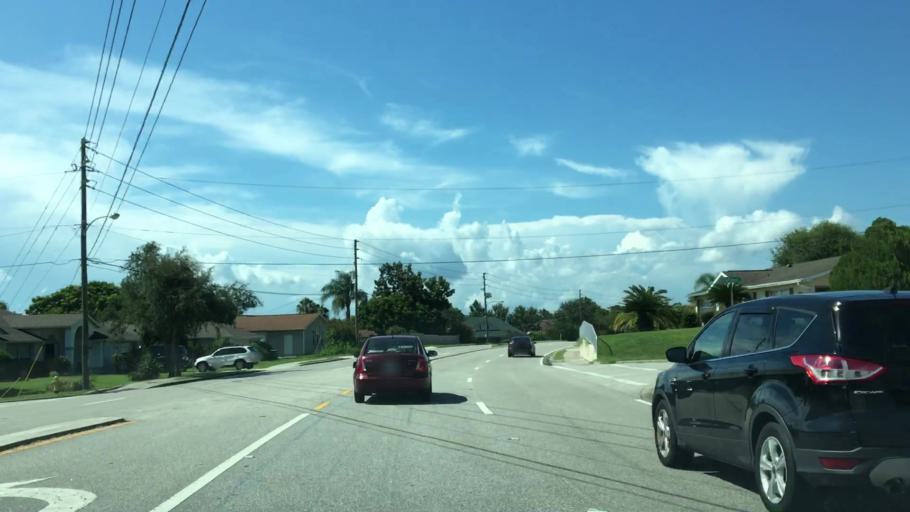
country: US
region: Florida
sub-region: Volusia County
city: Deltona
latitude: 28.9170
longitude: -81.2569
